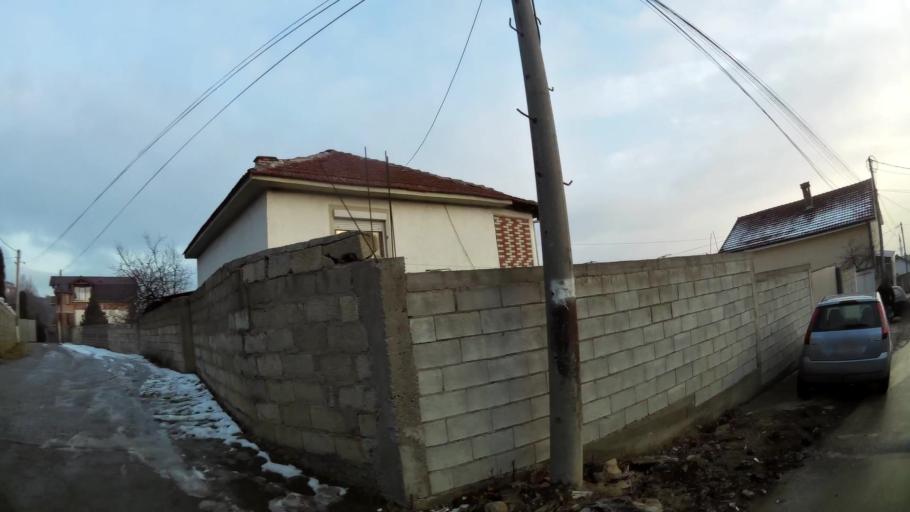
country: MK
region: Aracinovo
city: Arachinovo
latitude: 42.0326
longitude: 21.5660
